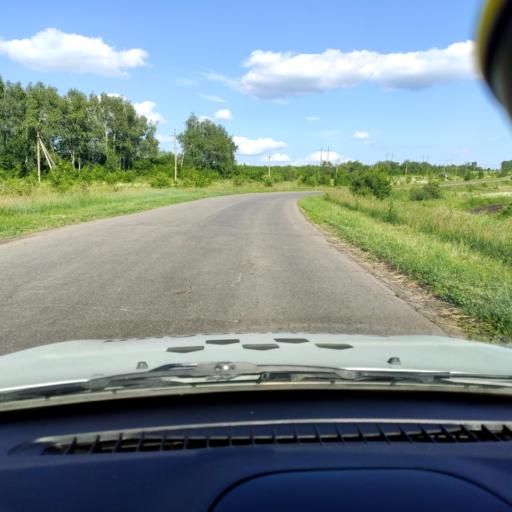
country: RU
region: Samara
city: Zhigulevsk
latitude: 53.3535
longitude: 49.3431
